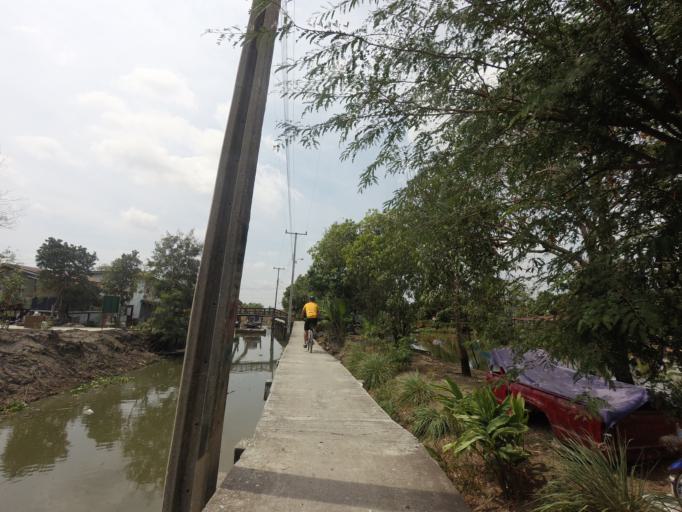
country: TH
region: Bangkok
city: Lat Krabang
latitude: 13.6619
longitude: 100.7617
